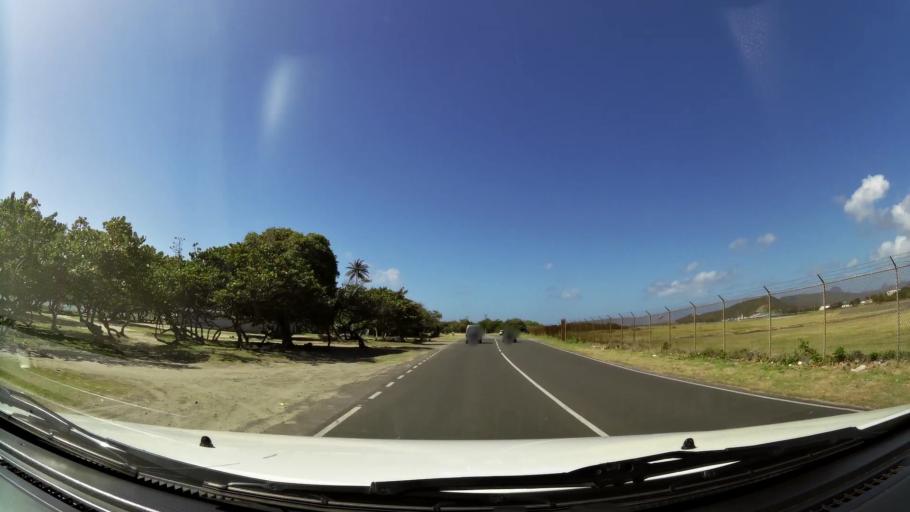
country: LC
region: Vieux-Fort
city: Vieux Fort
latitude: 13.7322
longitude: -60.9399
